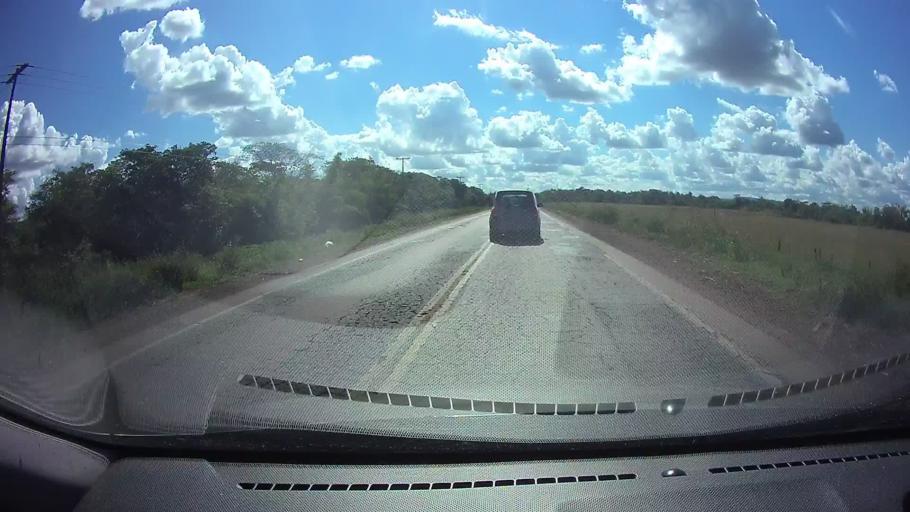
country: PY
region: Paraguari
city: La Colmena
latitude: -25.7526
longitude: -56.7805
